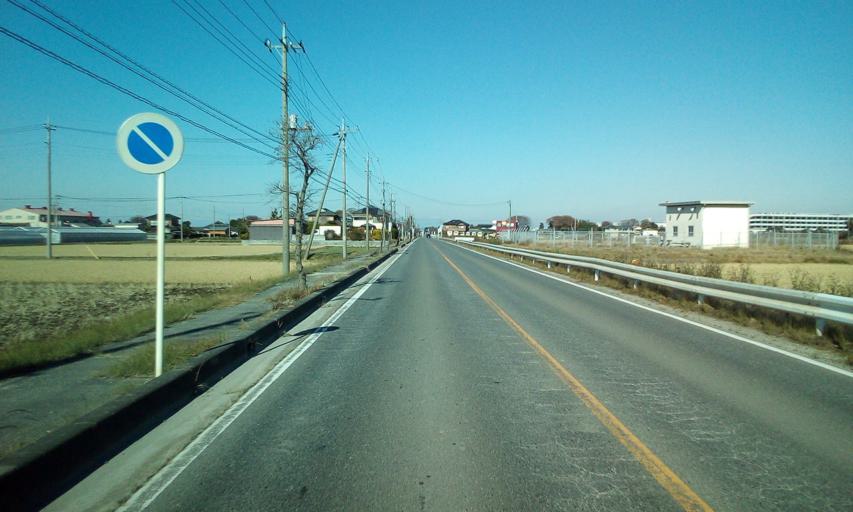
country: JP
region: Saitama
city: Kasukabe
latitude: 36.0248
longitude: 139.7892
